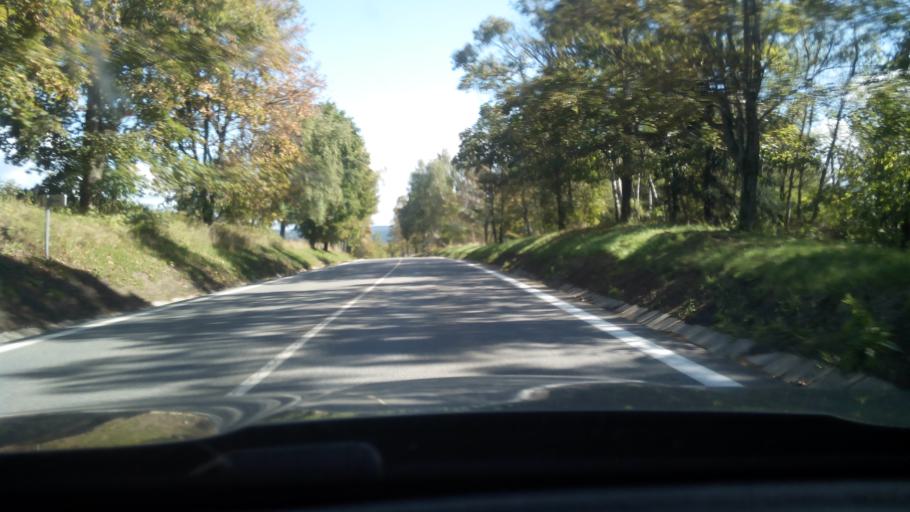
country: CZ
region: Jihocesky
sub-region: Okres Prachatice
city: Vimperk
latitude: 49.0613
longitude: 13.7578
